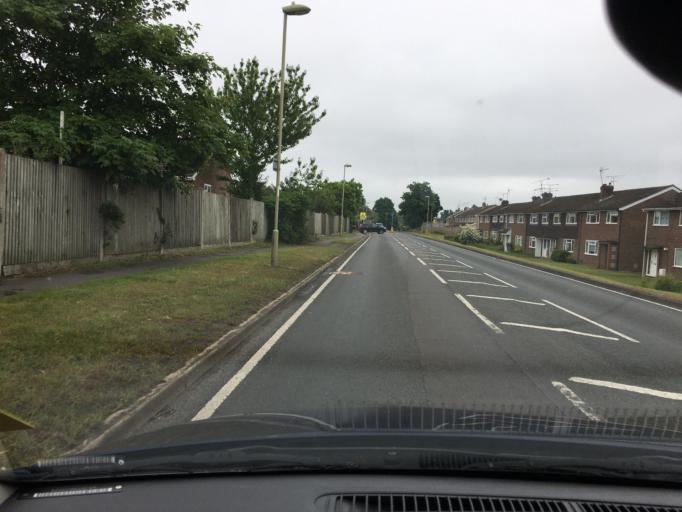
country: GB
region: England
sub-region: Bracknell Forest
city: Sandhurst
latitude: 51.3373
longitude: -0.7907
